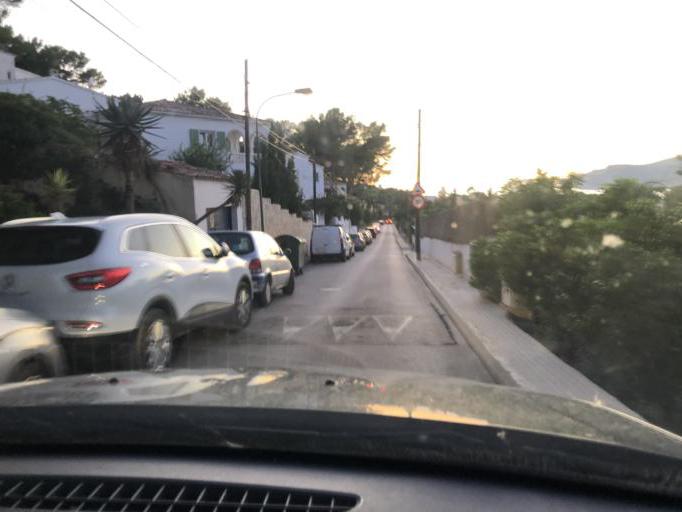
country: ES
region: Balearic Islands
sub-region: Illes Balears
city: Santa Ponsa
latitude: 39.5233
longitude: 2.4772
